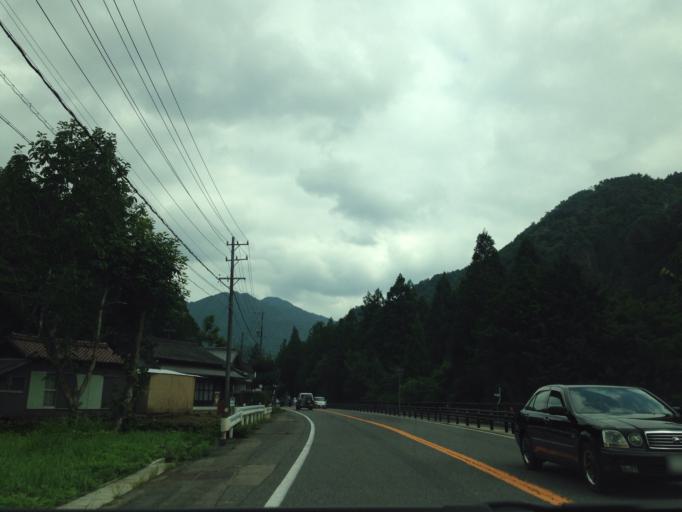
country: JP
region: Gifu
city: Mitake
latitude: 35.5892
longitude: 137.1713
